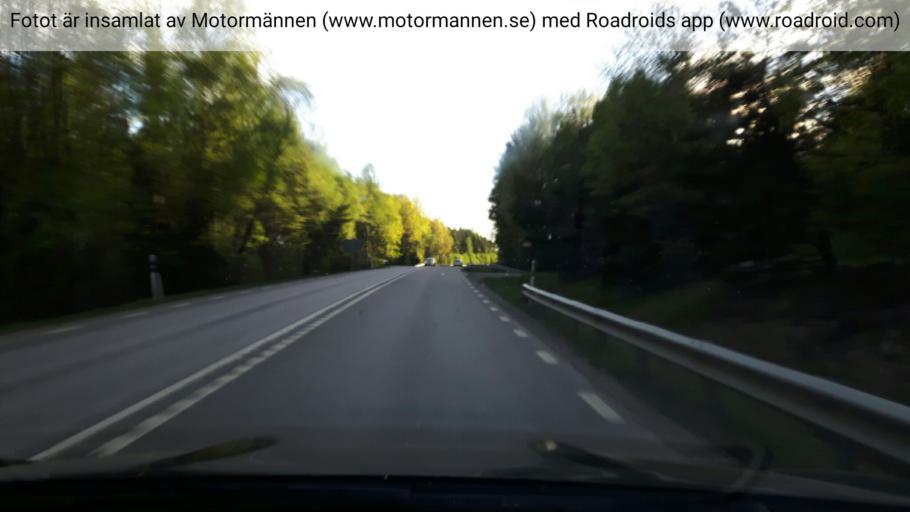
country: SE
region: Stockholm
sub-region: Osterakers Kommun
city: Akersberga
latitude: 59.4270
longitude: 18.2474
